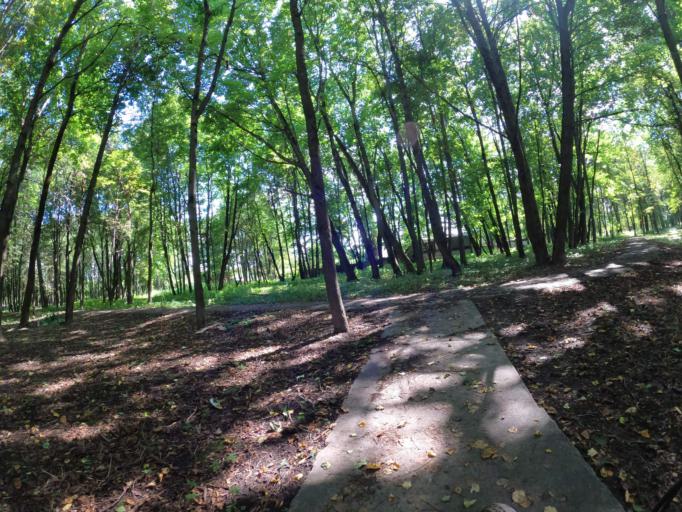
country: RU
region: Moskovskaya
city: Voskresensk
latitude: 55.2746
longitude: 38.6519
